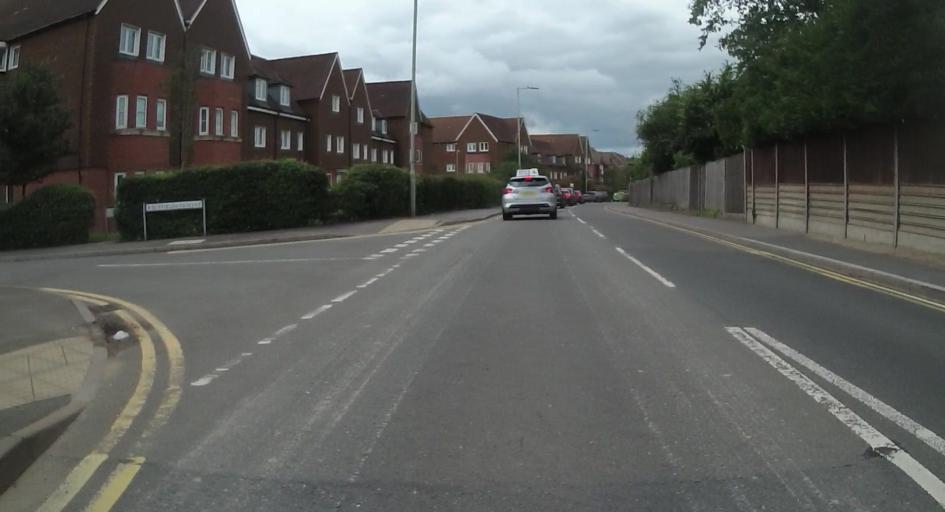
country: GB
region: England
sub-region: Wokingham
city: Wokingham
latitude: 51.4089
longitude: -0.8395
